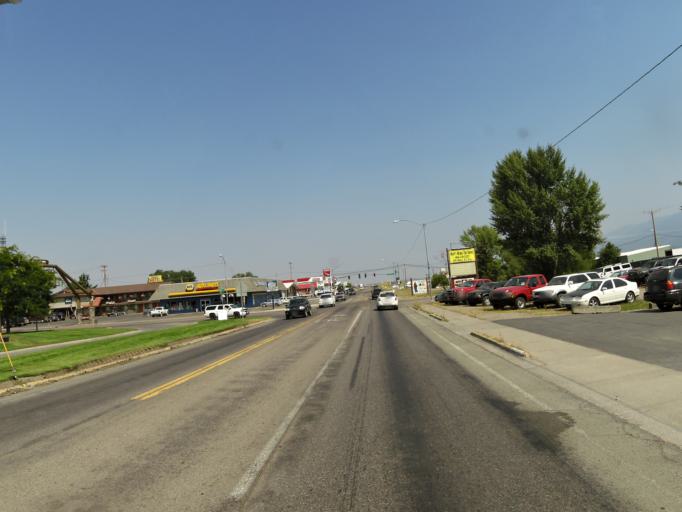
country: US
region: Montana
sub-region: Lake County
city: Ronan
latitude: 47.5281
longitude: -114.0971
